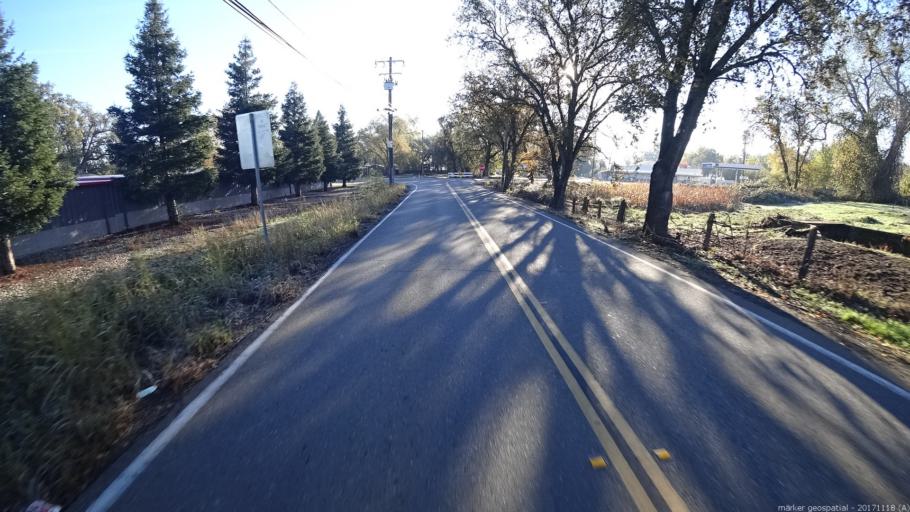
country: US
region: California
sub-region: Shasta County
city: Anderson
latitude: 40.4474
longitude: -122.2592
